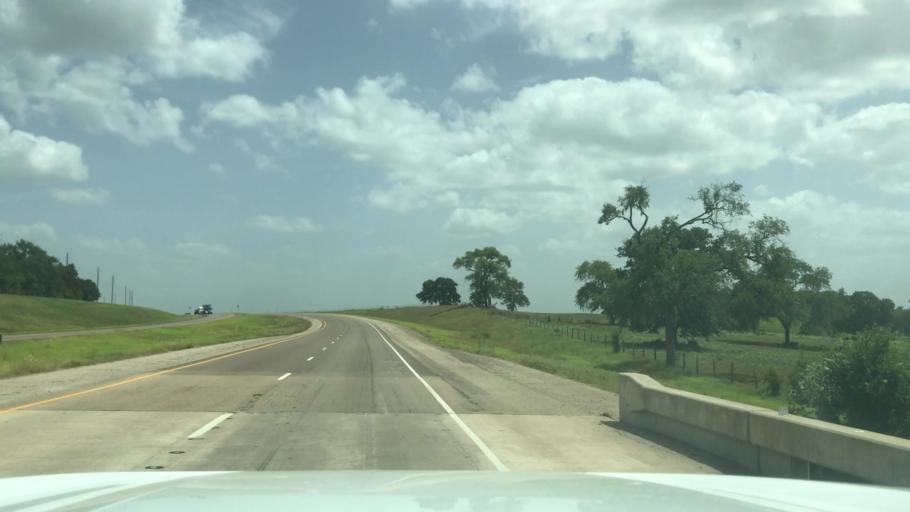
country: US
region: Texas
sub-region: Robertson County
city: Calvert
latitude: 31.0099
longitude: -96.7027
